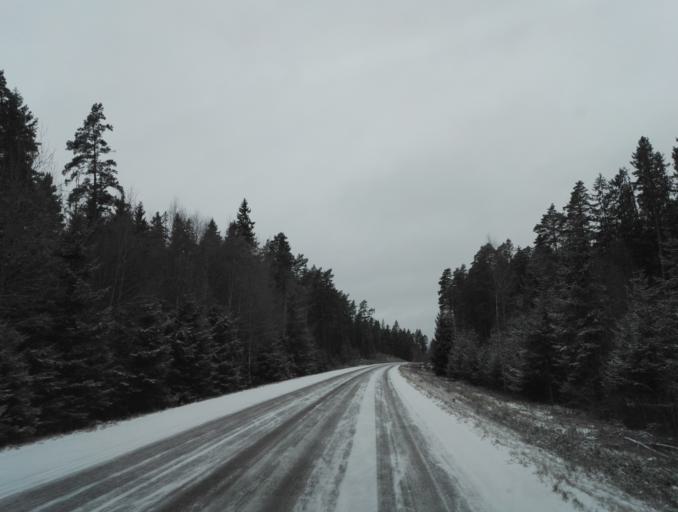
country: SE
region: Kronoberg
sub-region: Lessebo Kommun
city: Lessebo
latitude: 56.7312
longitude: 15.2267
